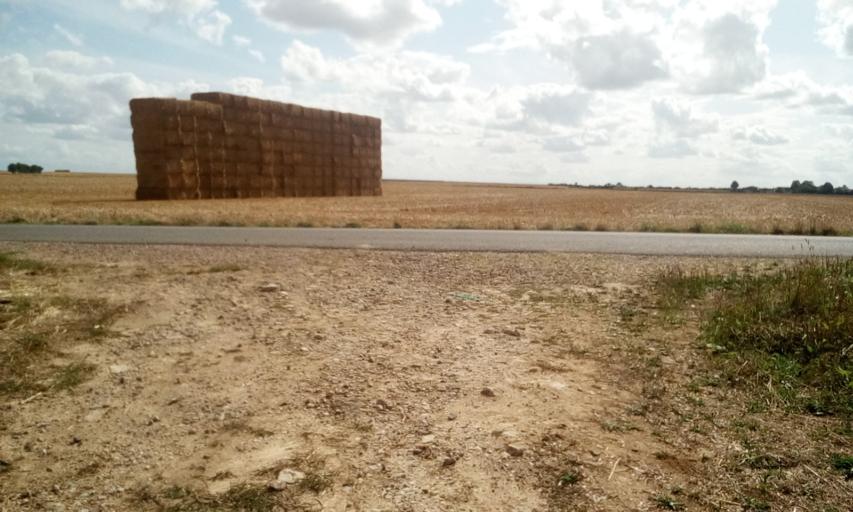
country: FR
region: Lower Normandy
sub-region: Departement du Calvados
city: Saint-Sylvain
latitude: 49.0888
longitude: -0.2060
